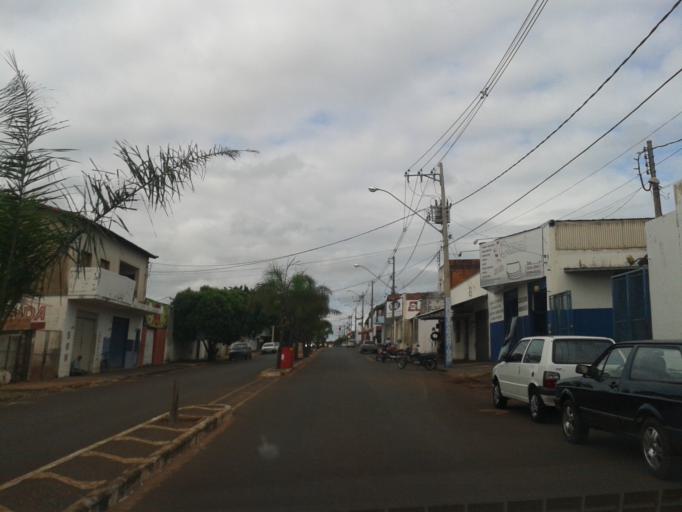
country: BR
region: Minas Gerais
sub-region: Ituiutaba
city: Ituiutaba
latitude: -18.9793
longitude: -49.4782
